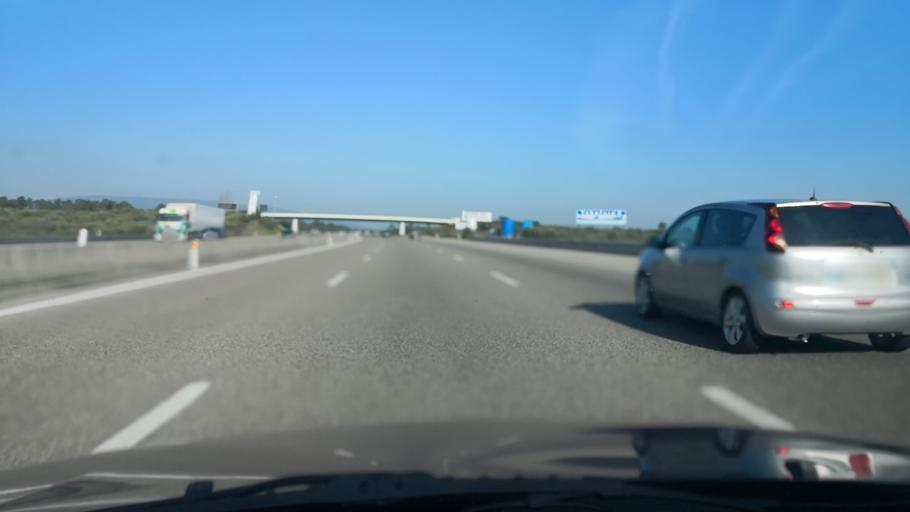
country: PT
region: Santarem
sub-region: Alcanena
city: Alcanena
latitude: 39.4186
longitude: -8.6326
